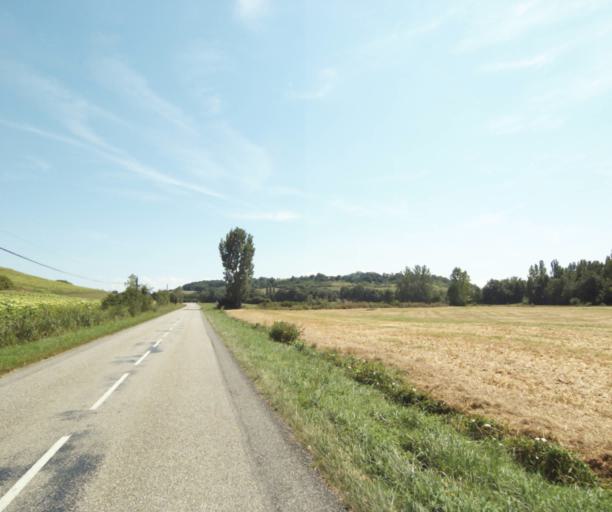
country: FR
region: Midi-Pyrenees
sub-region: Departement de l'Ariege
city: Lezat-sur-Leze
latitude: 43.2304
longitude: 1.3881
